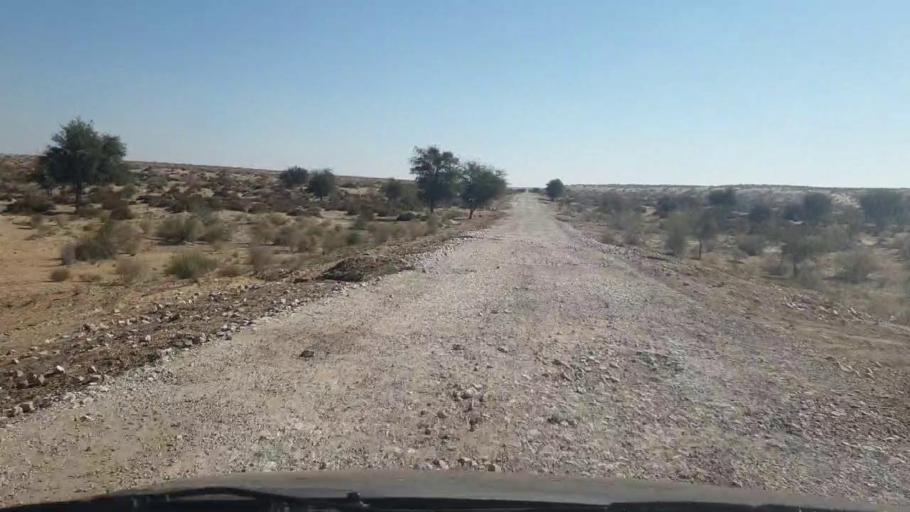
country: PK
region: Sindh
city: Bozdar
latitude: 27.0423
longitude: 68.6873
